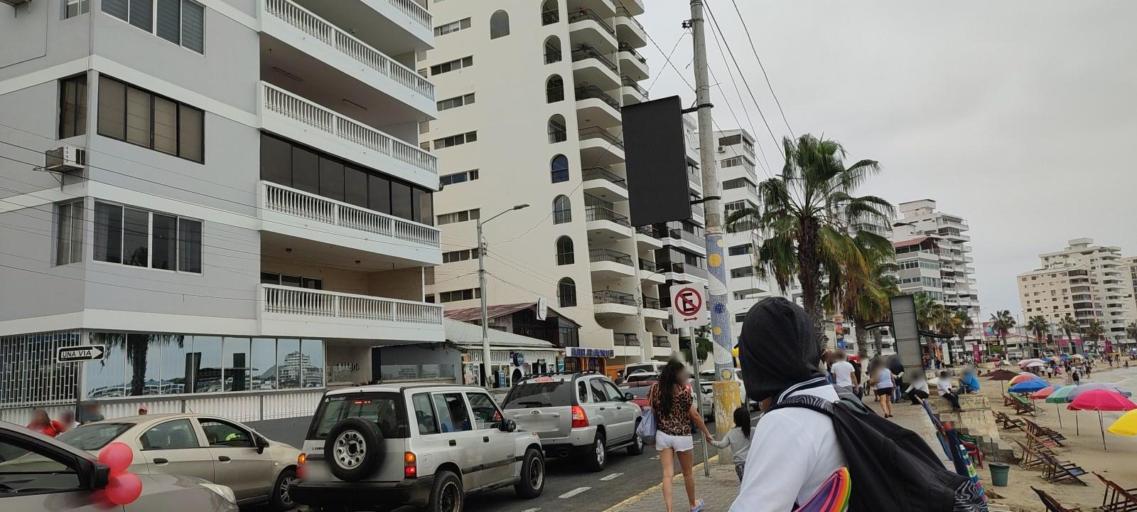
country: EC
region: Santa Elena
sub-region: Canton Salinas
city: Salinas
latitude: -2.2056
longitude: -80.9706
